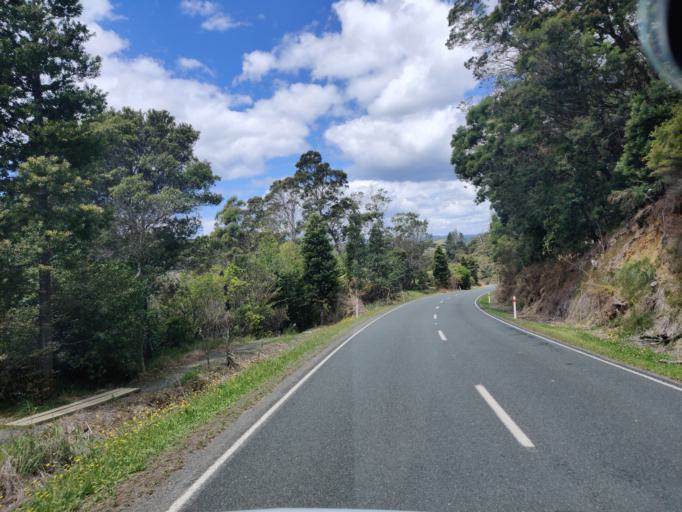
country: NZ
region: Northland
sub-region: Far North District
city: Paihia
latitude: -35.2696
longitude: 174.1354
